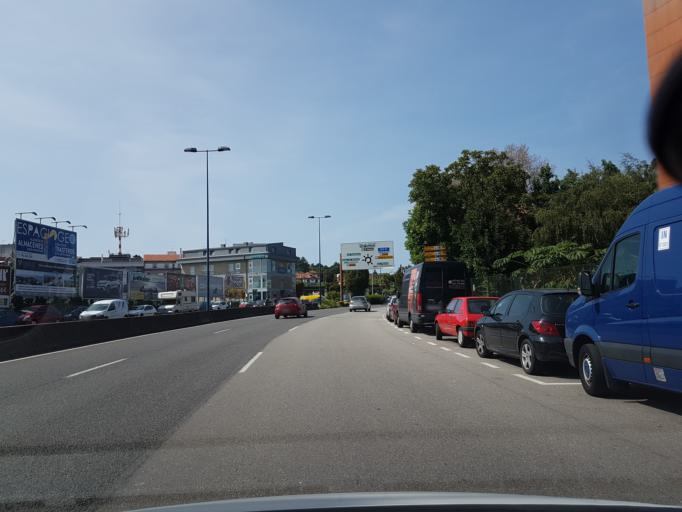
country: ES
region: Galicia
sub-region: Provincia de Pontevedra
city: Vigo
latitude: 42.2278
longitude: -8.7181
